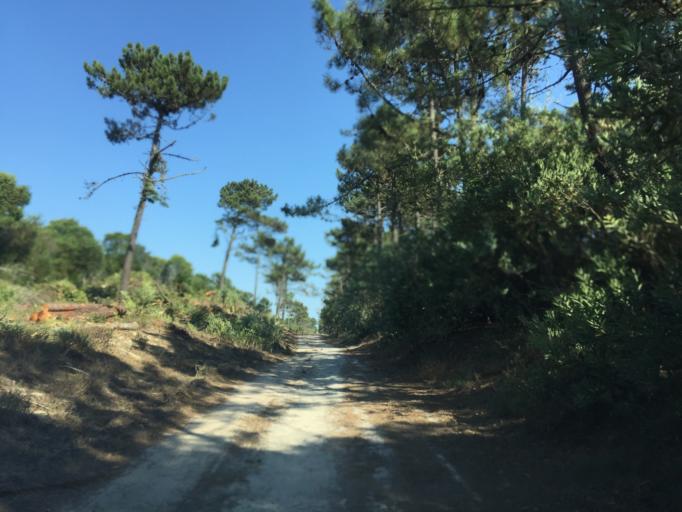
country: PT
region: Coimbra
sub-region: Figueira da Foz
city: Tavarede
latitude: 40.2631
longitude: -8.8620
